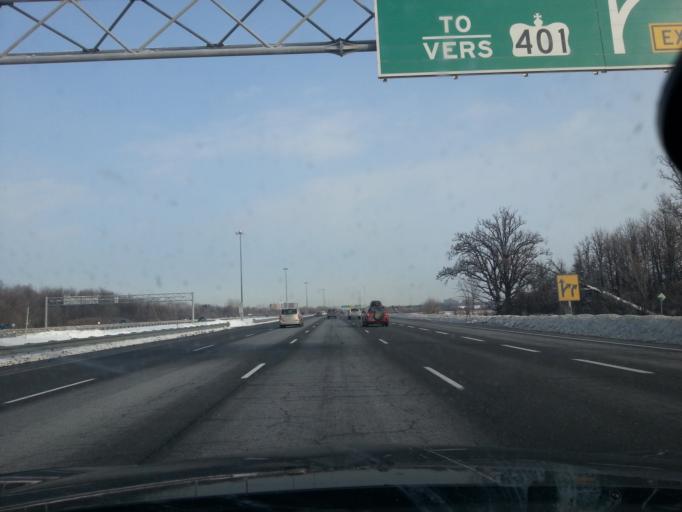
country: CA
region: Ontario
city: Bells Corners
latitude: 45.3412
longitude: -75.8310
